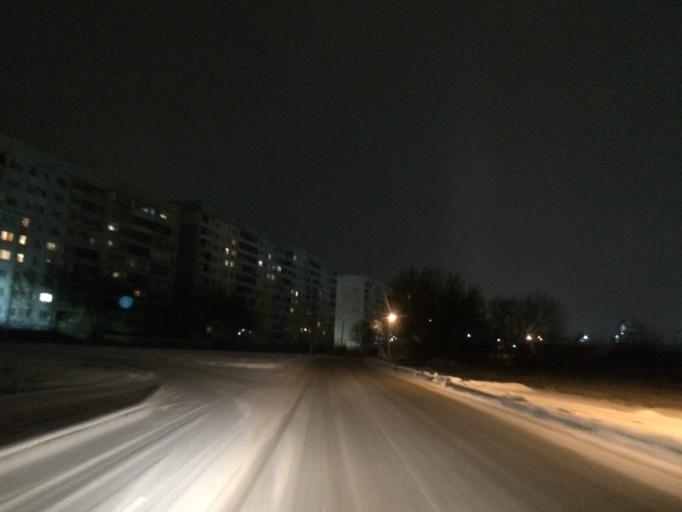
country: RU
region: Tula
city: Tula
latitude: 54.2078
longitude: 37.6427
